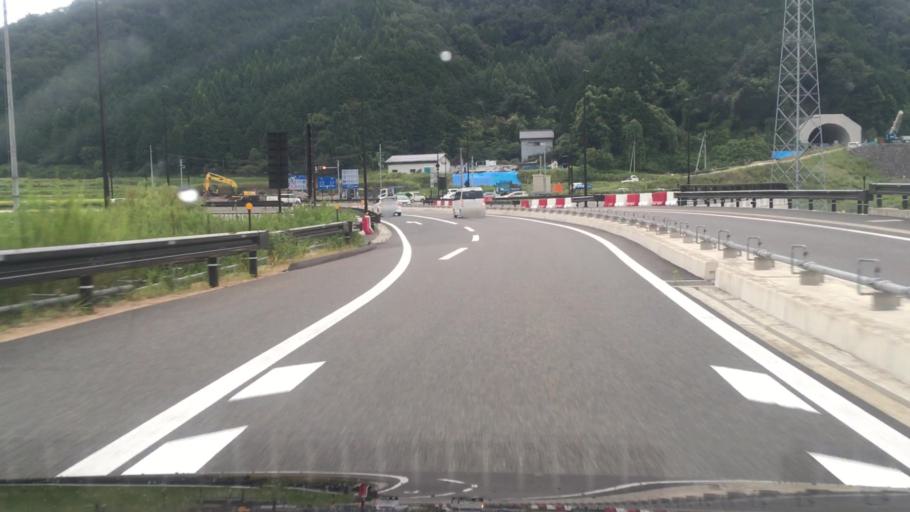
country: JP
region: Hyogo
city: Toyooka
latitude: 35.4674
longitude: 134.7616
